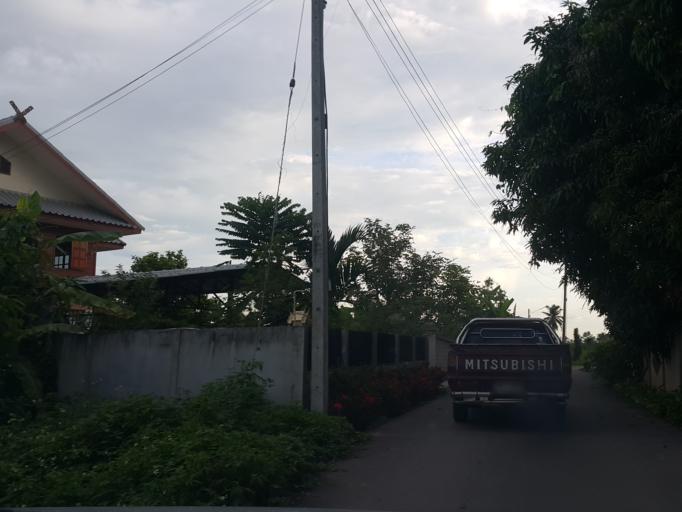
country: TH
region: Chiang Mai
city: San Sai
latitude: 18.8844
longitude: 99.0724
